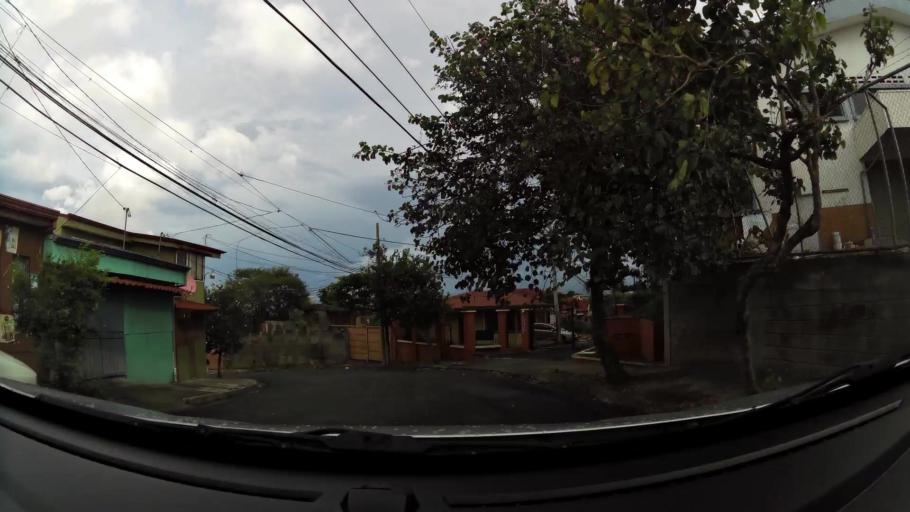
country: CR
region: San Jose
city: San Jose
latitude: 9.9388
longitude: -84.0919
